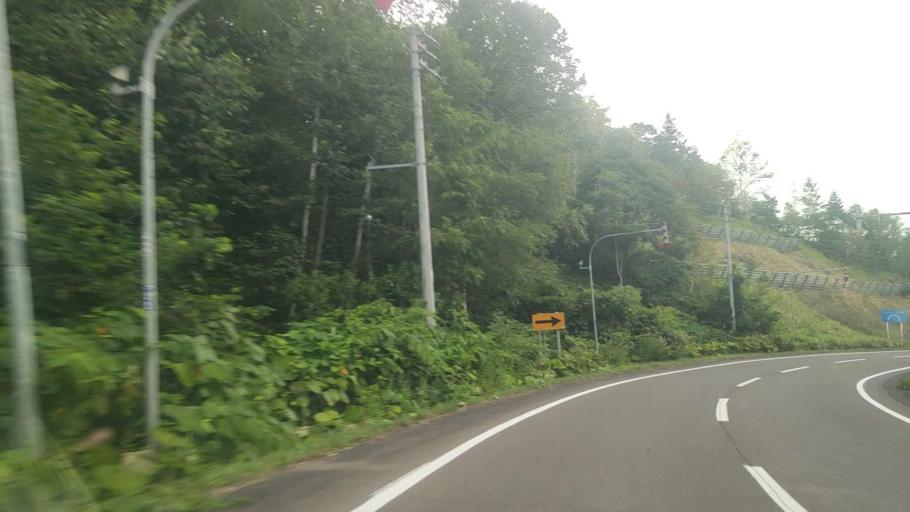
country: JP
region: Hokkaido
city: Bibai
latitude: 43.1681
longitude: 142.0787
